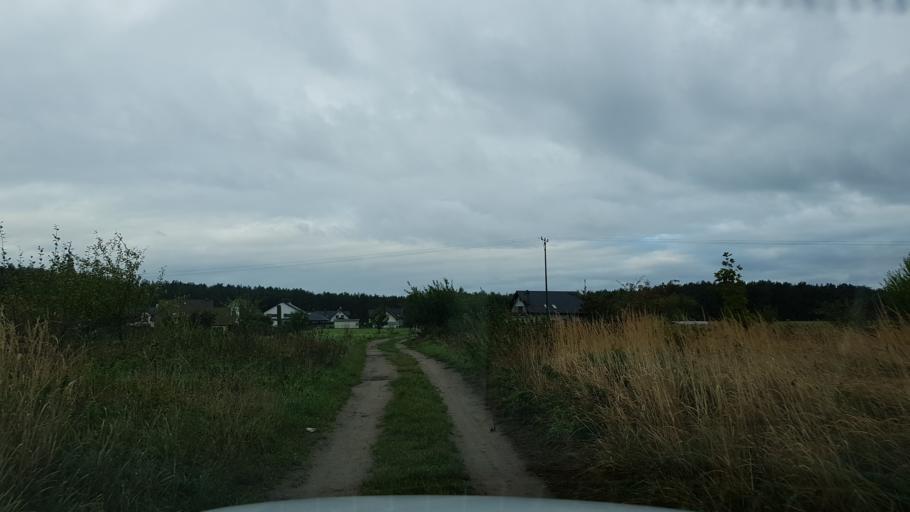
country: PL
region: West Pomeranian Voivodeship
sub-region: Powiat kamienski
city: Wolin
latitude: 53.8379
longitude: 14.6064
